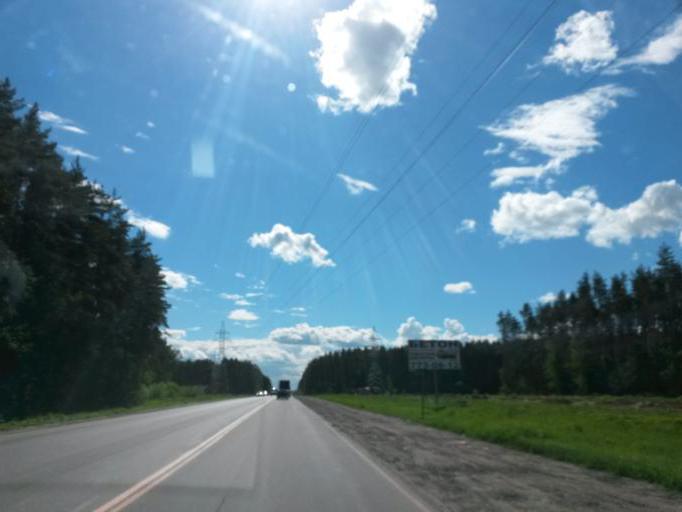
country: RU
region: Moskovskaya
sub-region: Podol'skiy Rayon
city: Podol'sk
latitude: 55.3980
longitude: 37.5814
